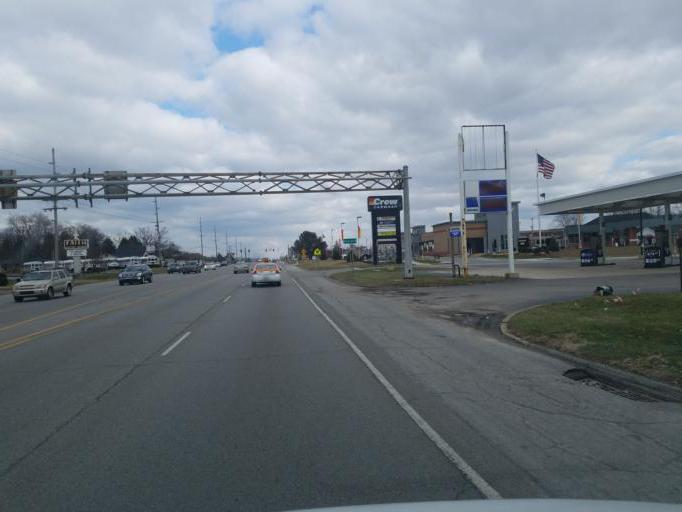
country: US
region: Indiana
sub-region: Hendricks County
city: Avon
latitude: 39.7627
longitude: -86.3988
